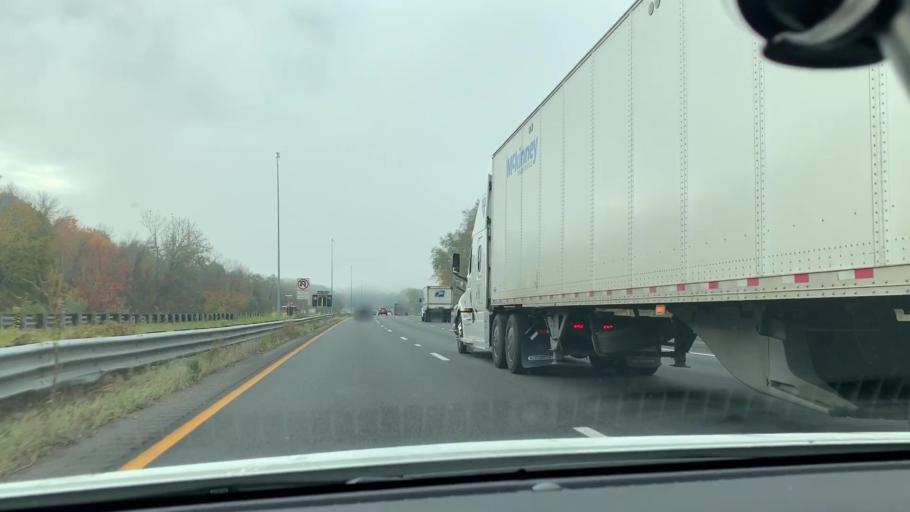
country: US
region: Massachusetts
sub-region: Hampden County
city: Longmeadow
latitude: 42.0359
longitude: -72.5889
